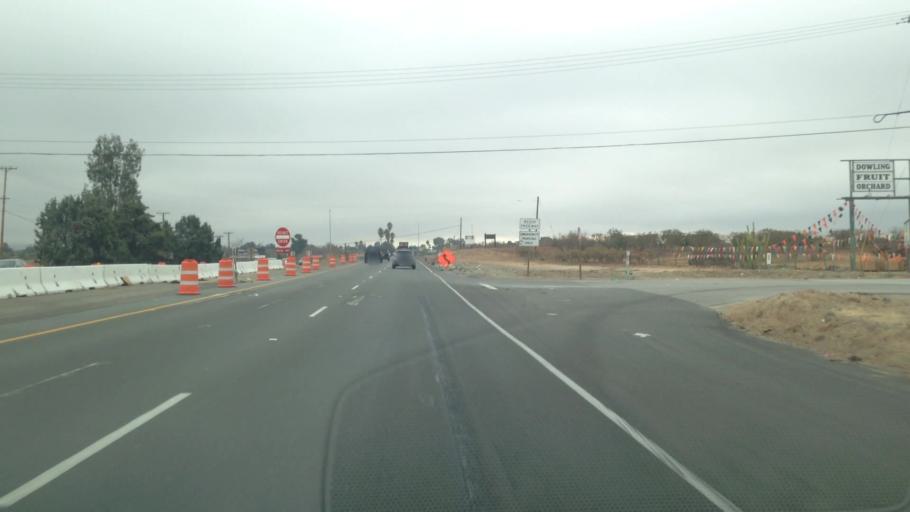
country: US
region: California
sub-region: Riverside County
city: Beaumont
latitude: 33.9333
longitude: -116.9994
